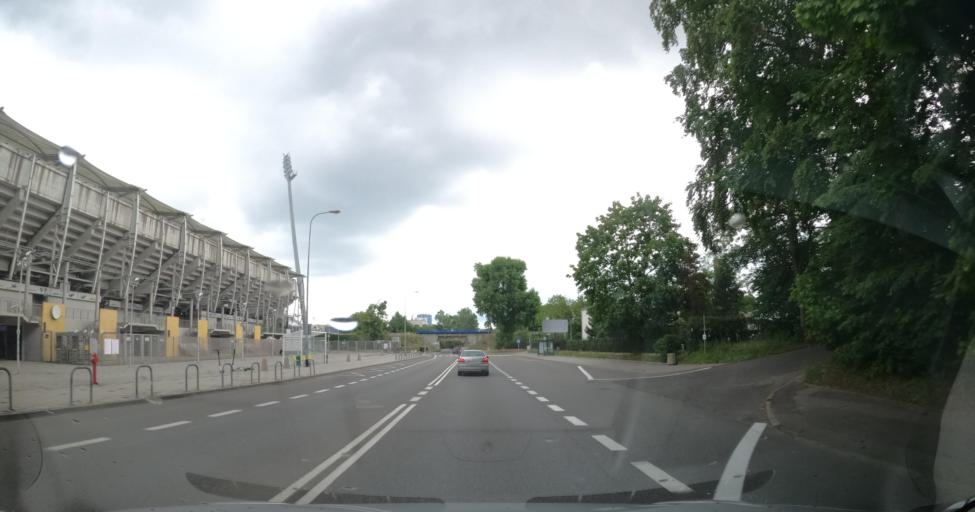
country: PL
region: Pomeranian Voivodeship
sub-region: Gdynia
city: Gdynia
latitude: 54.4923
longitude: 18.5301
